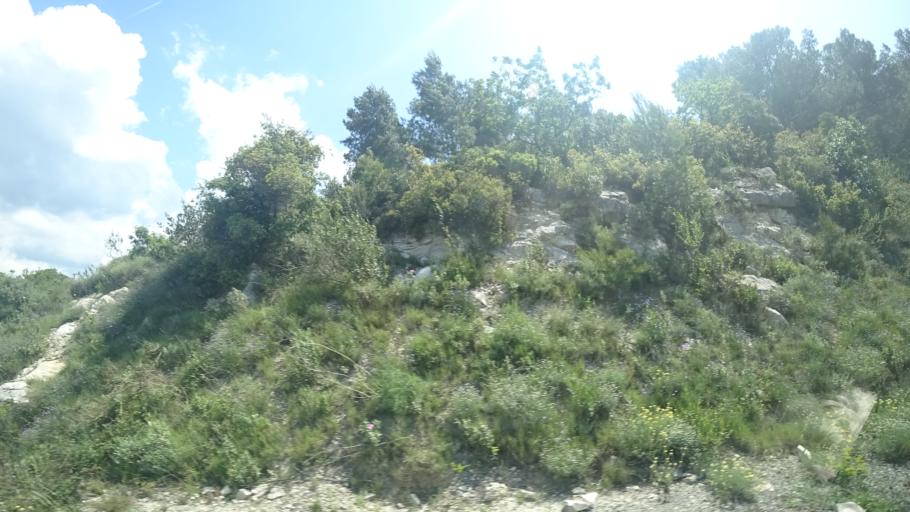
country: FR
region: Languedoc-Roussillon
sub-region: Departement de l'Herault
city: Olonzac
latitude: 43.3520
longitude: 2.7565
